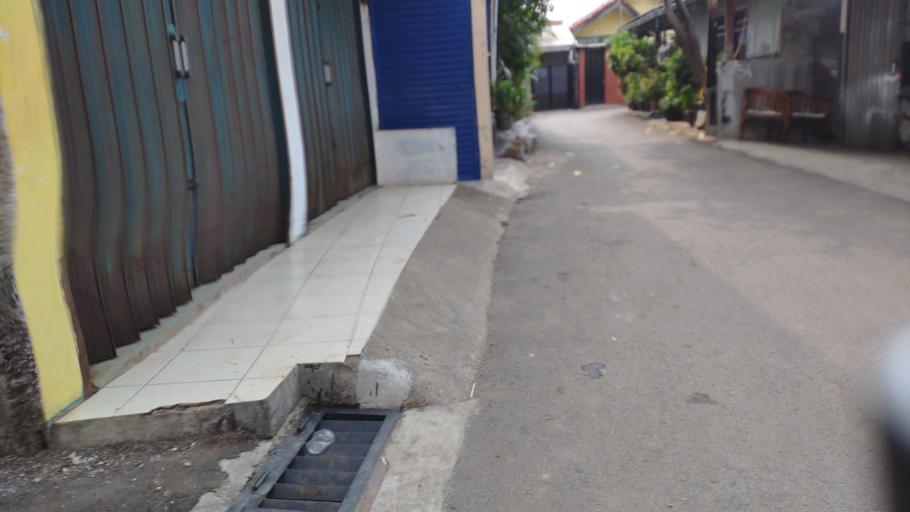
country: ID
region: West Java
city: Pamulang
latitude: -6.3147
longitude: 106.8053
